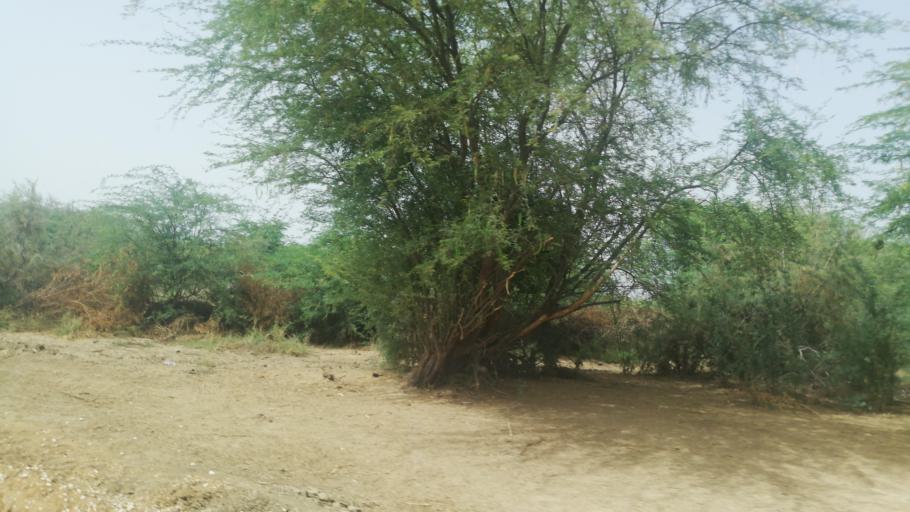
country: SN
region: Saint-Louis
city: Saint-Louis
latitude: 16.0635
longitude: -16.3145
